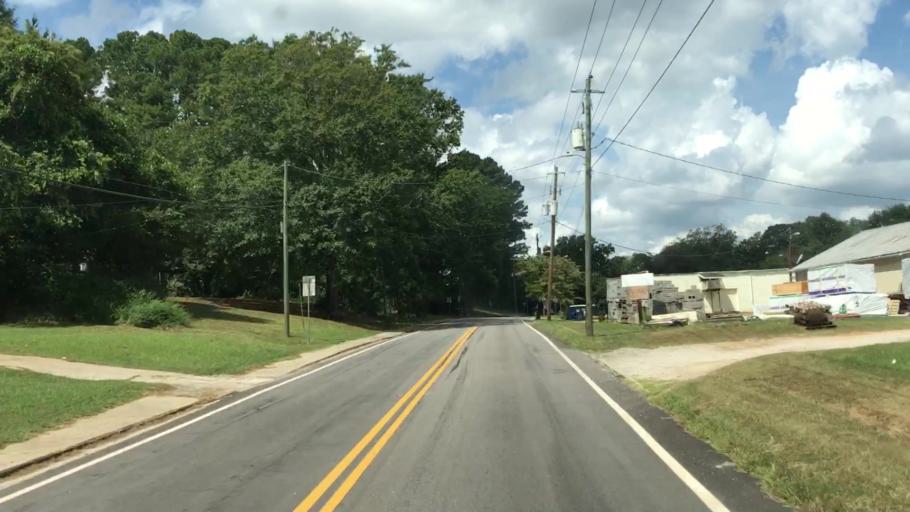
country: US
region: Georgia
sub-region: Greene County
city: Greensboro
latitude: 33.5746
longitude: -83.1768
